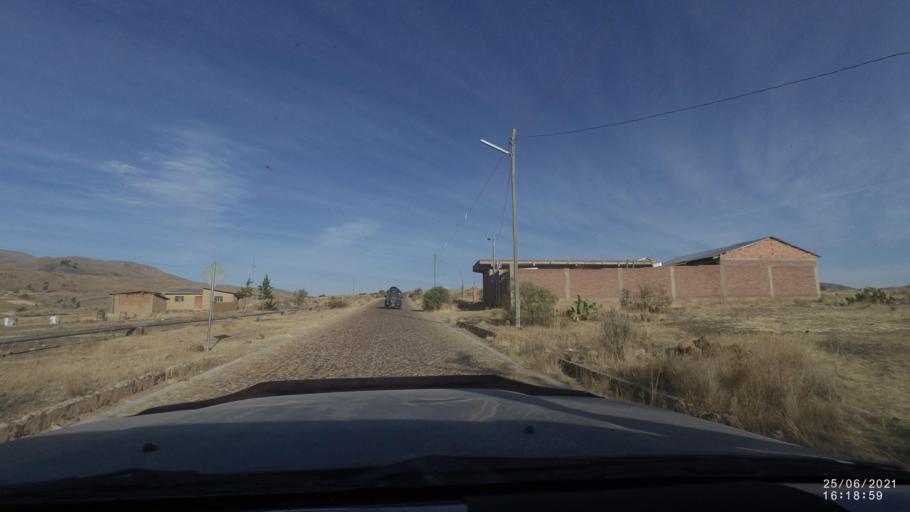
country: BO
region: Cochabamba
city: Cliza
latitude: -17.7373
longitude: -65.8493
